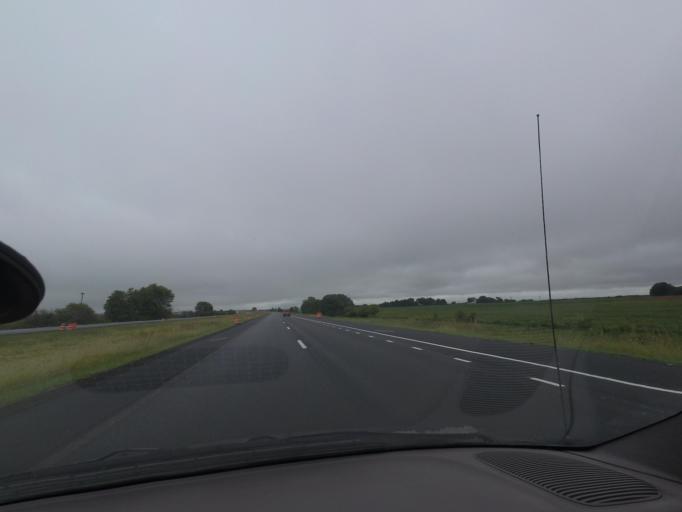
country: US
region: Illinois
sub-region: Macon County
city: Harristown
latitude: 39.8328
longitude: -89.1490
